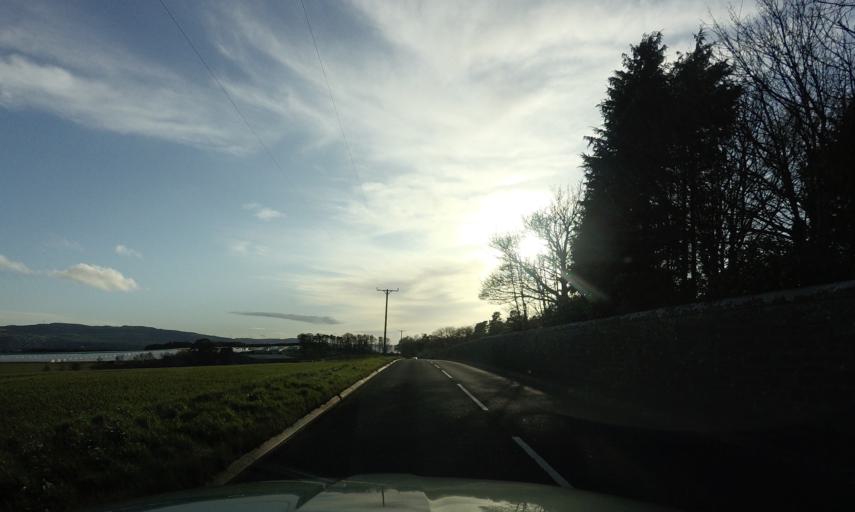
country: GB
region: Scotland
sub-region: Perth and Kinross
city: Errol
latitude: 56.3862
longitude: -3.2272
